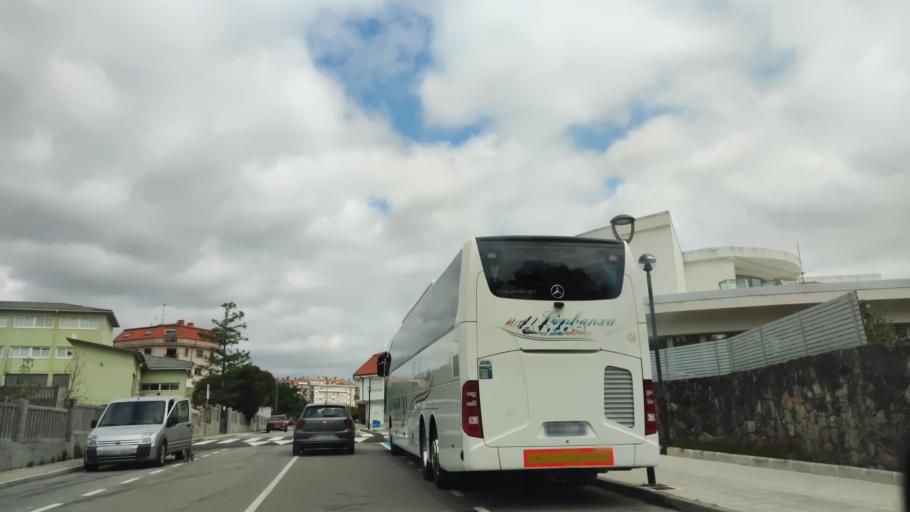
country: ES
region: Galicia
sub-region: Provincia da Coruna
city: Boiro
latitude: 42.6418
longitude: -8.8916
